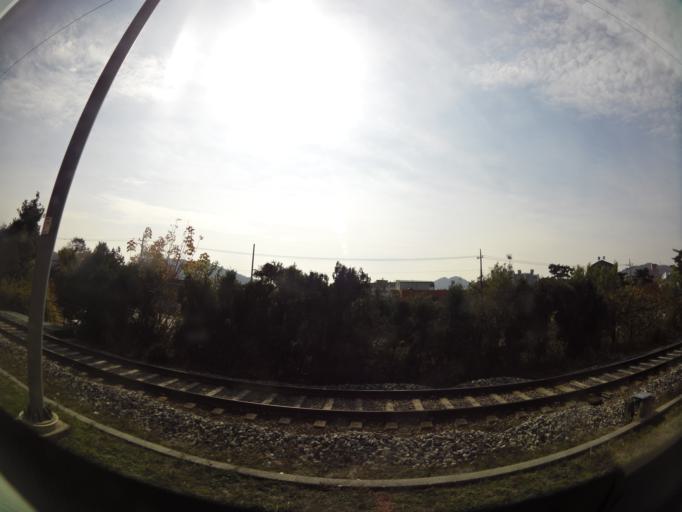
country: KR
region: Daejeon
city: Sintansin
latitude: 36.5316
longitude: 127.3693
